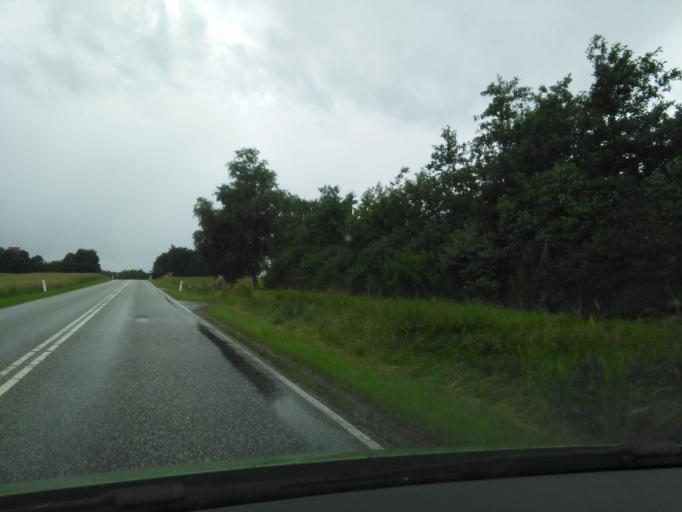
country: DK
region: Central Jutland
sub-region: Skanderborg Kommune
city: Ry
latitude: 56.0028
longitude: 9.7725
